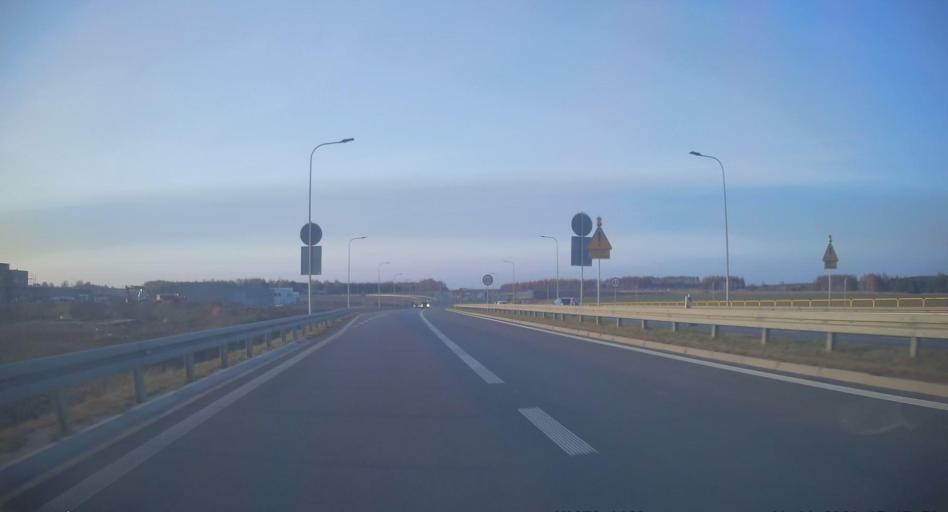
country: PL
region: Silesian Voivodeship
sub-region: Powiat klobucki
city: Kamyk
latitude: 50.8494
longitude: 19.0404
